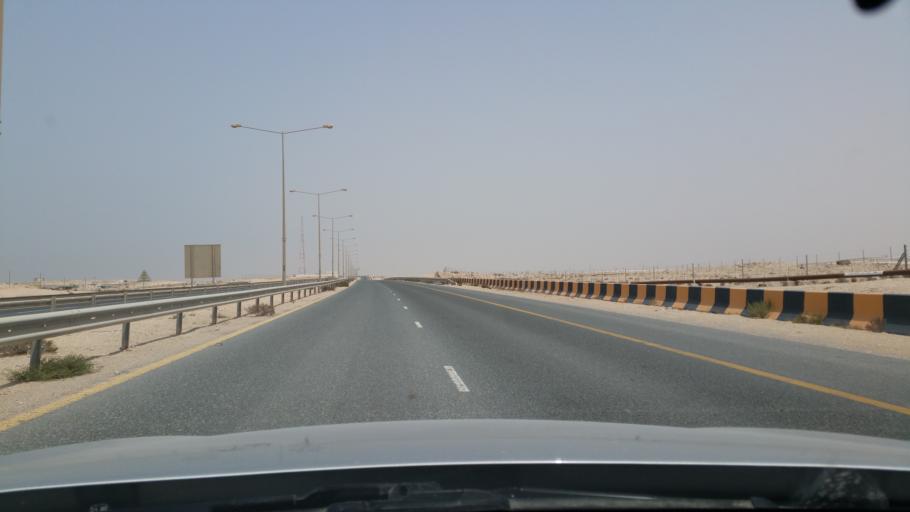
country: QA
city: Umm Bab
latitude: 25.3013
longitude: 50.7925
